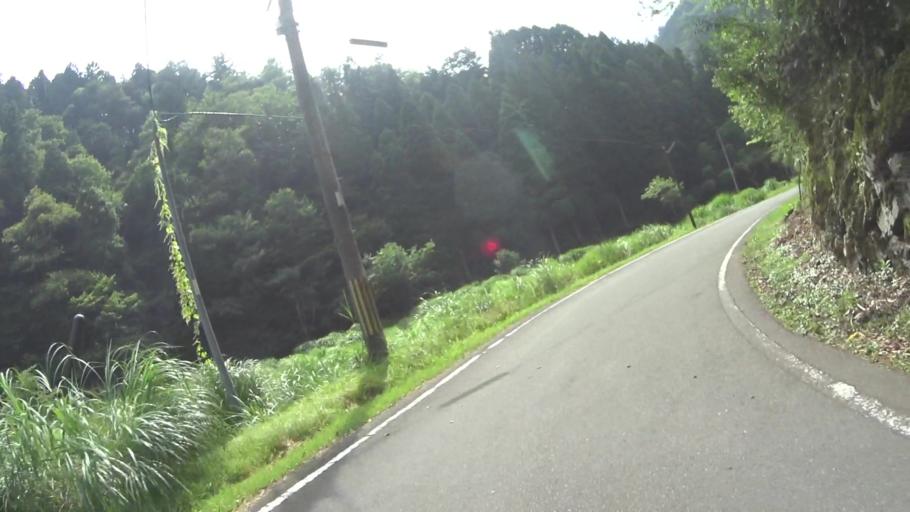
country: JP
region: Fukui
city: Obama
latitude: 35.3430
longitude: 135.6496
